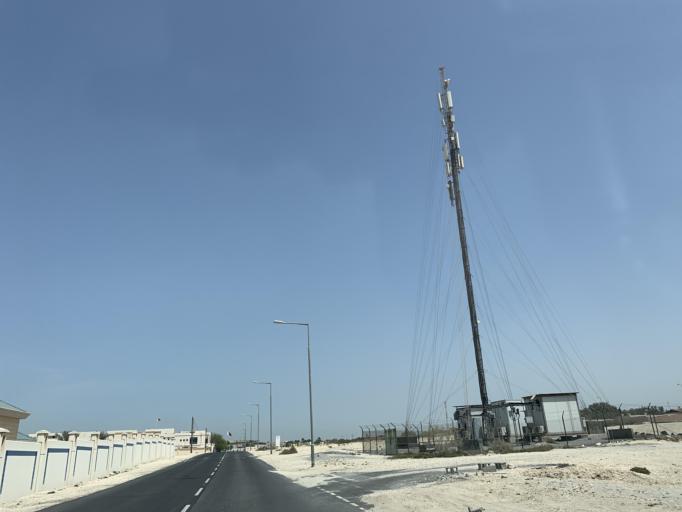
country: BH
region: Northern
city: Ar Rifa'
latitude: 26.1469
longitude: 50.5435
